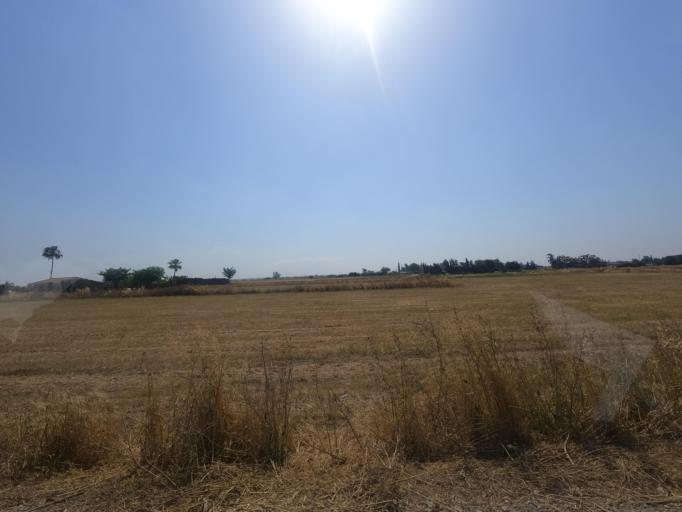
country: CY
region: Ammochostos
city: Avgorou
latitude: 35.0477
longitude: 33.8516
